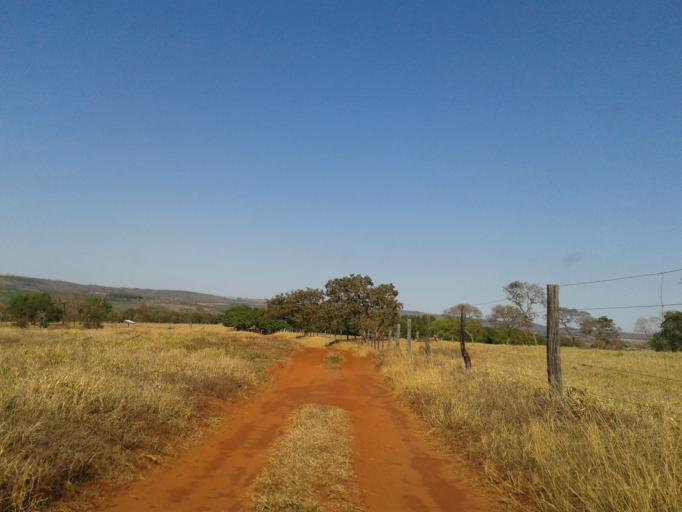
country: BR
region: Minas Gerais
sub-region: Ituiutaba
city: Ituiutaba
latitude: -19.0485
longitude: -49.2880
